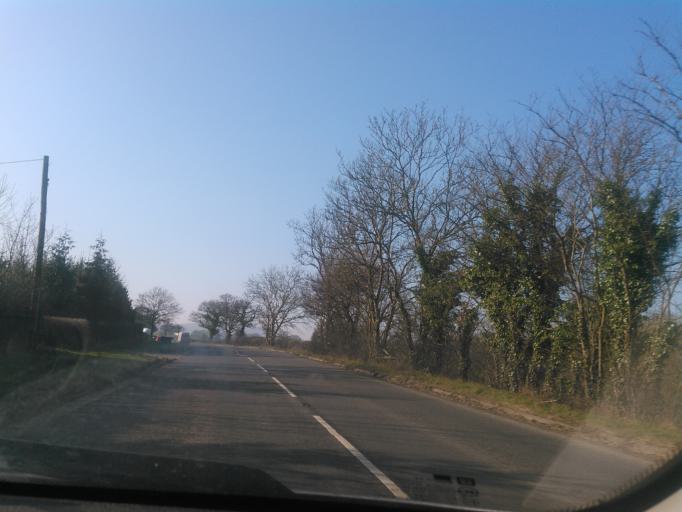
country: GB
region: England
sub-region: Shropshire
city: Church Stretton
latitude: 52.5711
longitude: -2.7812
